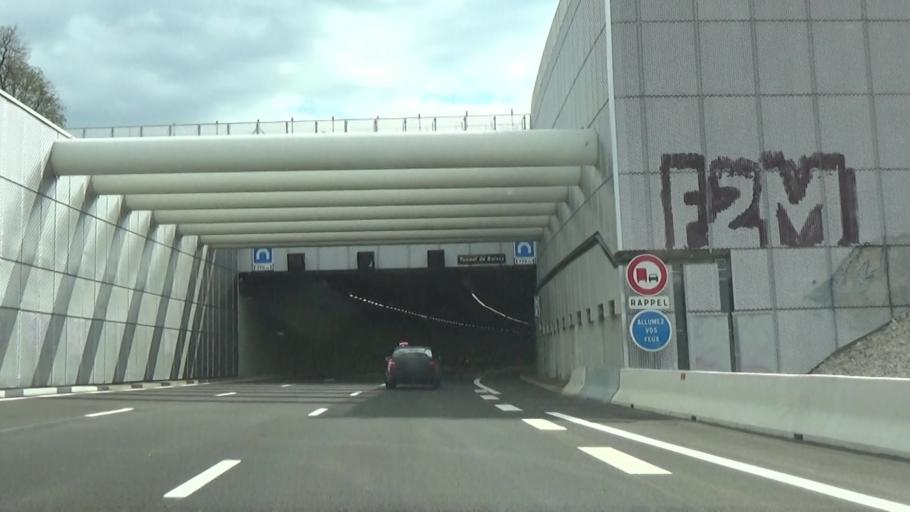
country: FR
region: Ile-de-France
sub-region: Departement du Val-de-Marne
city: Boissy-Saint-Leger
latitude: 48.7532
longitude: 2.5120
